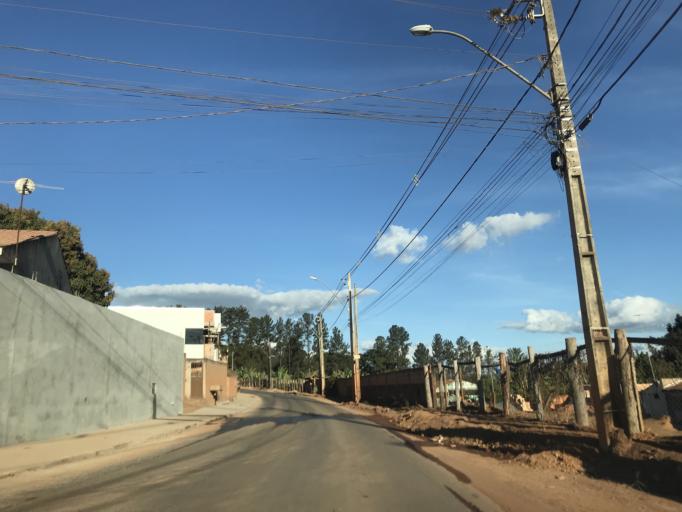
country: BR
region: Federal District
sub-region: Brasilia
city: Brasilia
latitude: -15.8828
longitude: -47.7747
